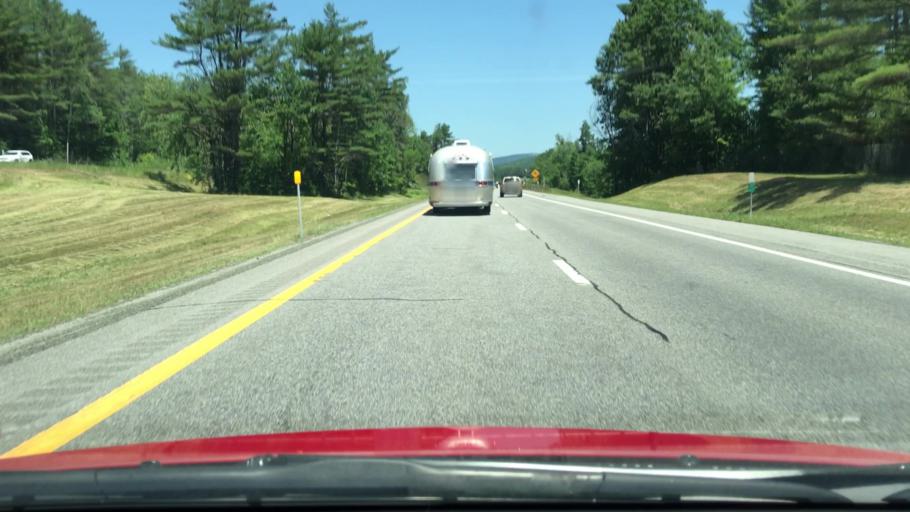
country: US
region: New York
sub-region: Essex County
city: Elizabethtown
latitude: 44.2974
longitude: -73.5315
